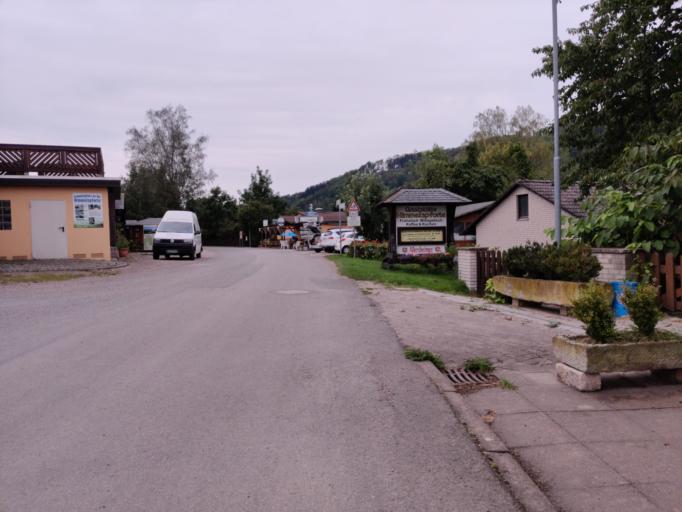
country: DE
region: Lower Saxony
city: Bodenwerder
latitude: 51.9595
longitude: 9.5055
